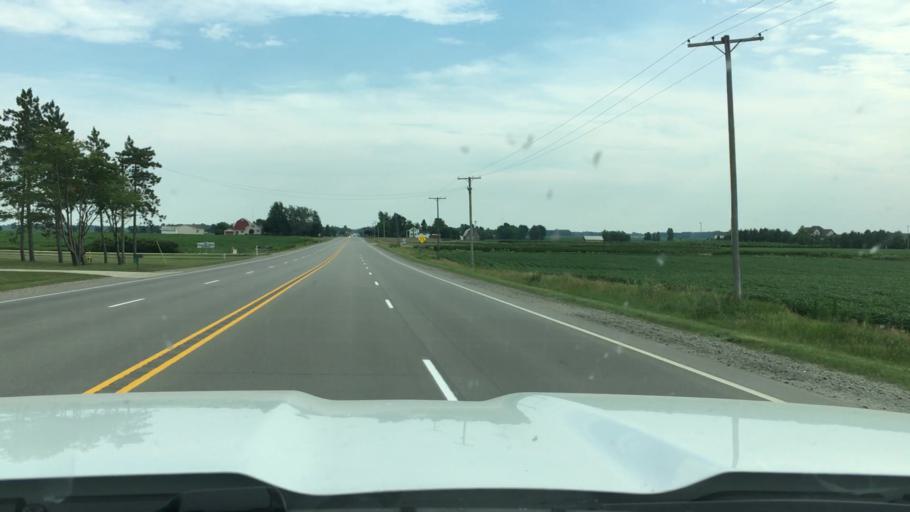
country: US
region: Michigan
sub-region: Sanilac County
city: Marlette
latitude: 43.3800
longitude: -83.0859
